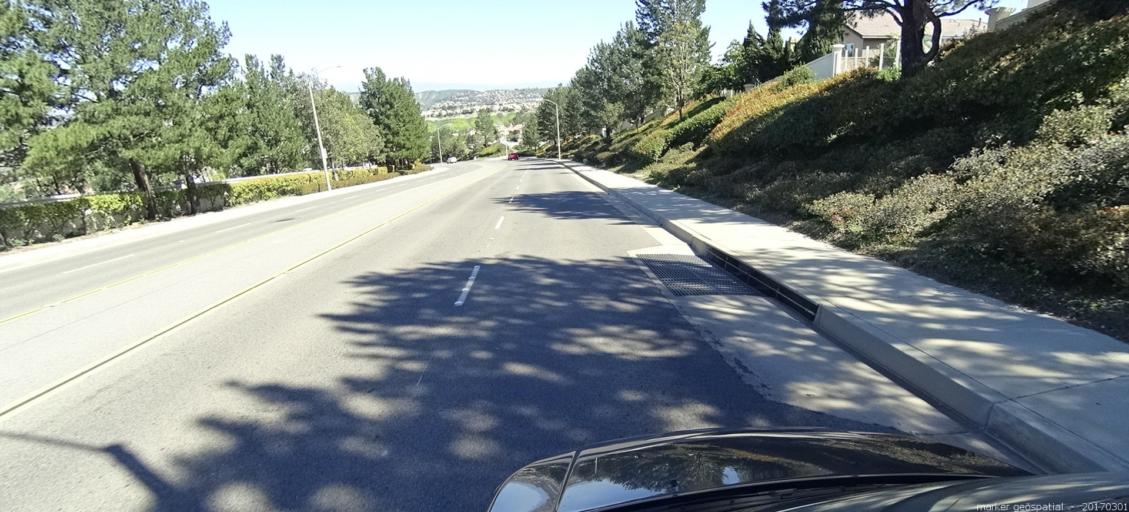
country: US
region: California
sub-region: Orange County
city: Yorba Linda
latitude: 33.8518
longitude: -117.7360
